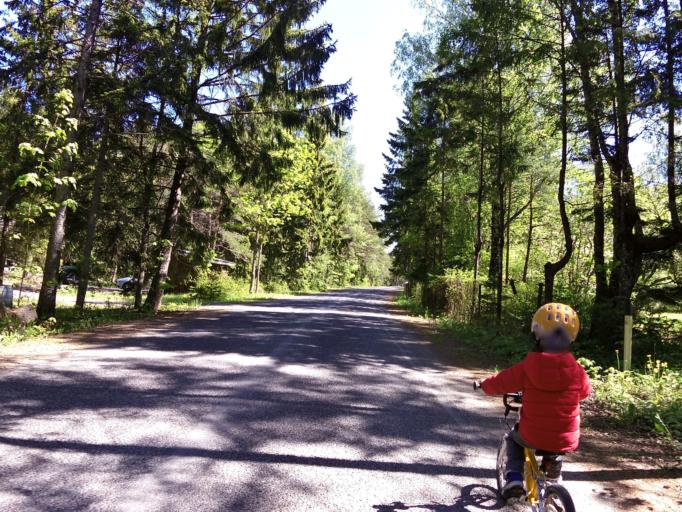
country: EE
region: Harju
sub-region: Paldiski linn
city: Paldiski
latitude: 59.2688
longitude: 23.7506
